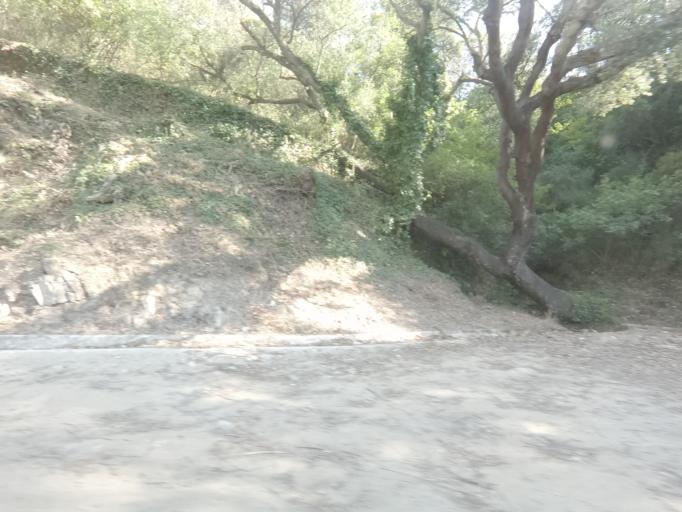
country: PT
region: Vila Real
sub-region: Sabrosa
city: Vilela
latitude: 41.2002
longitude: -7.5598
